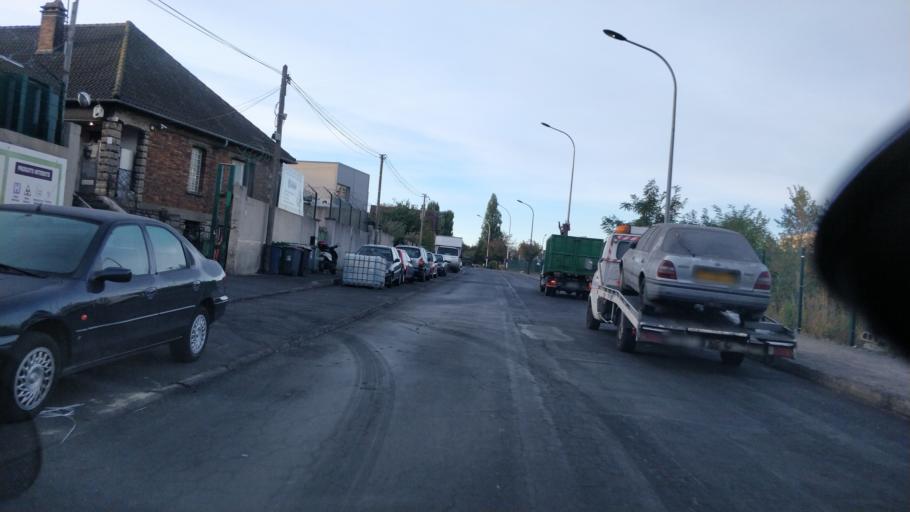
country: FR
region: Ile-de-France
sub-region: Departement des Hauts-de-Seine
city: Chatillon
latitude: 48.7991
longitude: 2.2980
